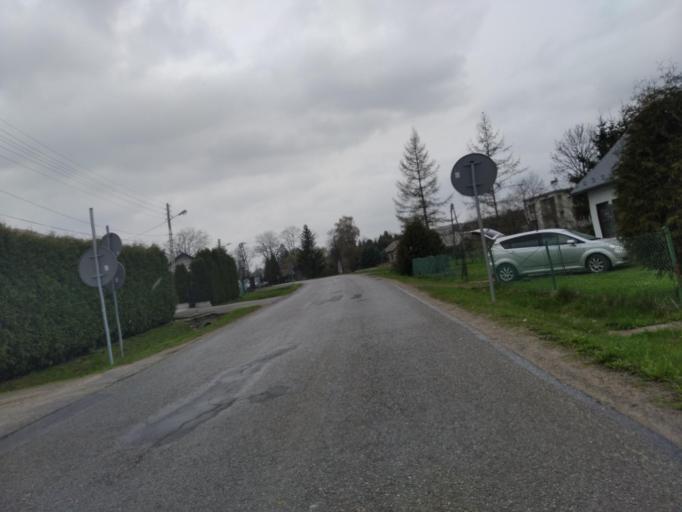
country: PL
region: Subcarpathian Voivodeship
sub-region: Powiat sanocki
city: Strachocina
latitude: 49.6095
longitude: 22.0808
